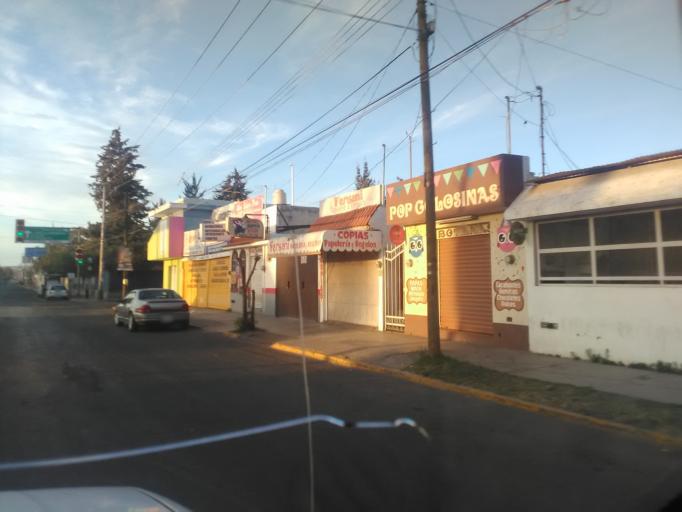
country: MX
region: Durango
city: Victoria de Durango
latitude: 24.0041
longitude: -104.6625
